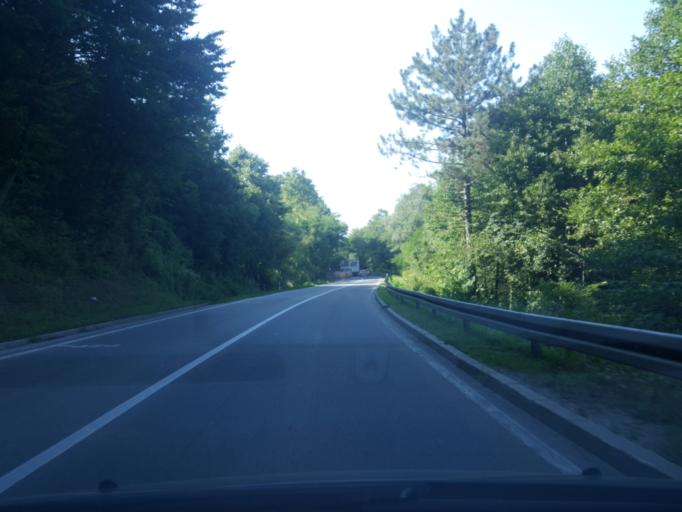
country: RS
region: Central Serbia
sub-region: Moravicki Okrug
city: Gornji Milanovac
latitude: 44.0765
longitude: 20.4864
